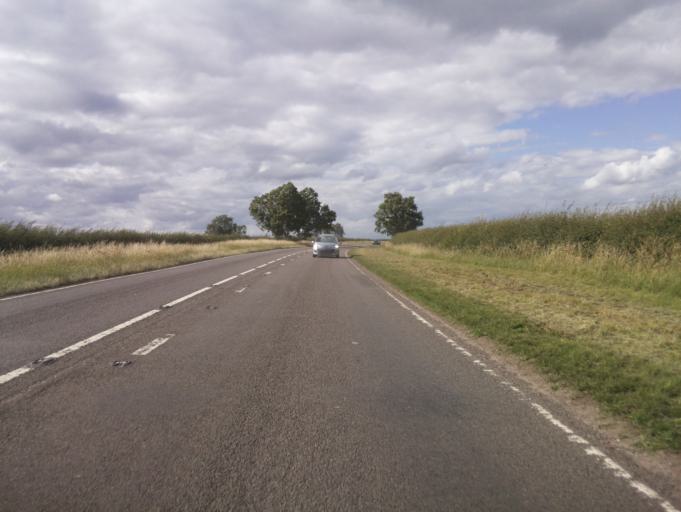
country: GB
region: England
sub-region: Warwickshire
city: Hartshill
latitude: 52.5852
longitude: -1.4789
